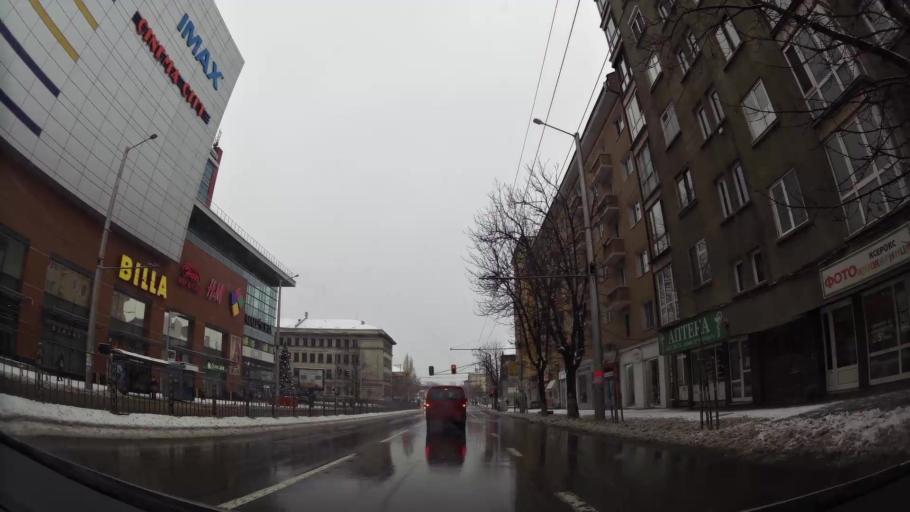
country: BG
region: Sofia-Capital
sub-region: Stolichna Obshtina
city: Sofia
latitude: 42.6978
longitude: 23.3096
